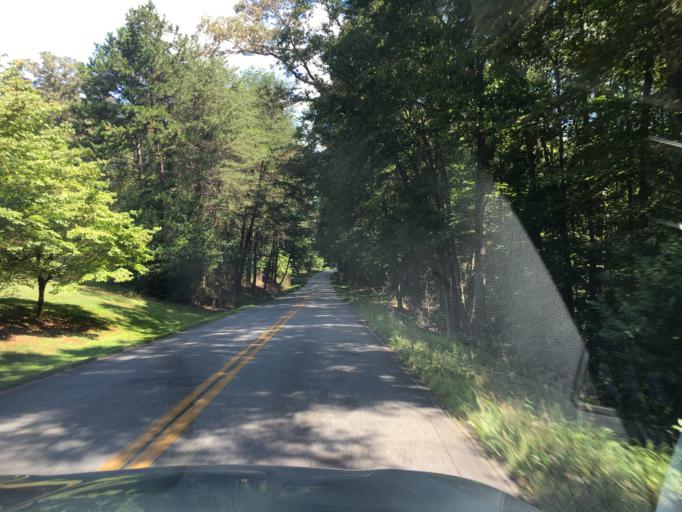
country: US
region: South Carolina
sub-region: Spartanburg County
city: Wellford
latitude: 34.8957
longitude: -82.0606
